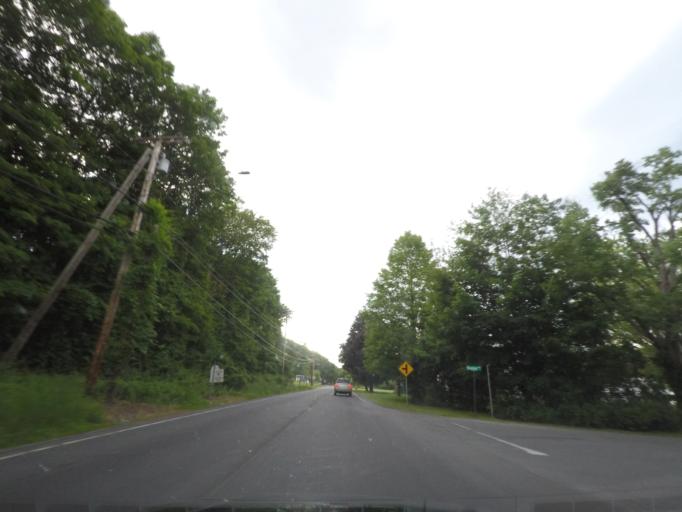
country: US
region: New York
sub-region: Dutchess County
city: Pine Plains
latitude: 41.9854
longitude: -73.6703
